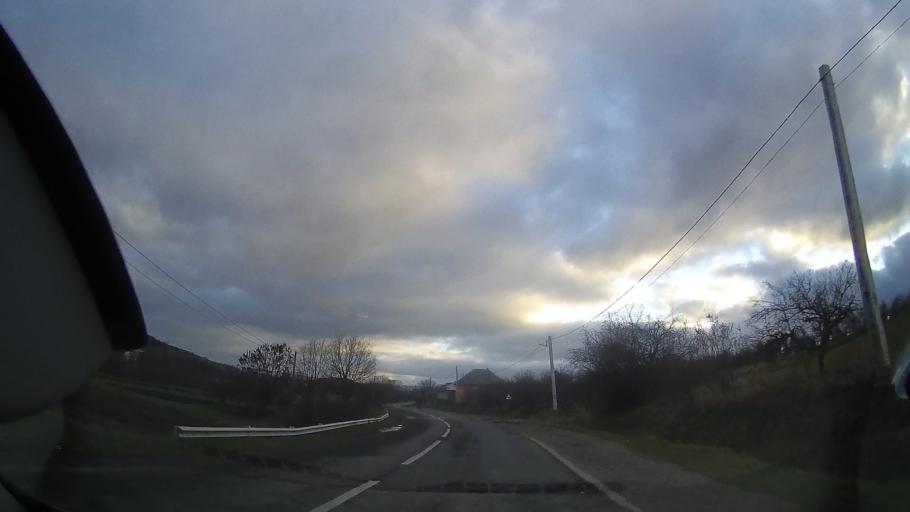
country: RO
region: Cluj
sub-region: Comuna Sancraiu
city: Sancraiu
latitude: 46.8085
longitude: 22.9935
